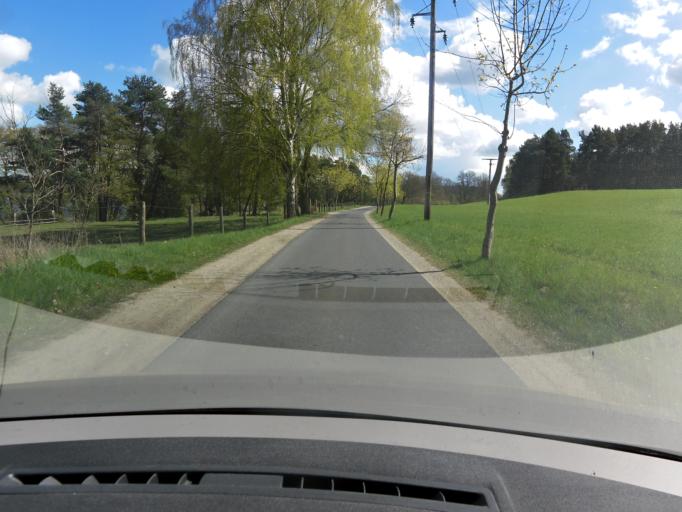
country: DE
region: Mecklenburg-Vorpommern
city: Malchow
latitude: 53.4646
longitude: 12.3541
